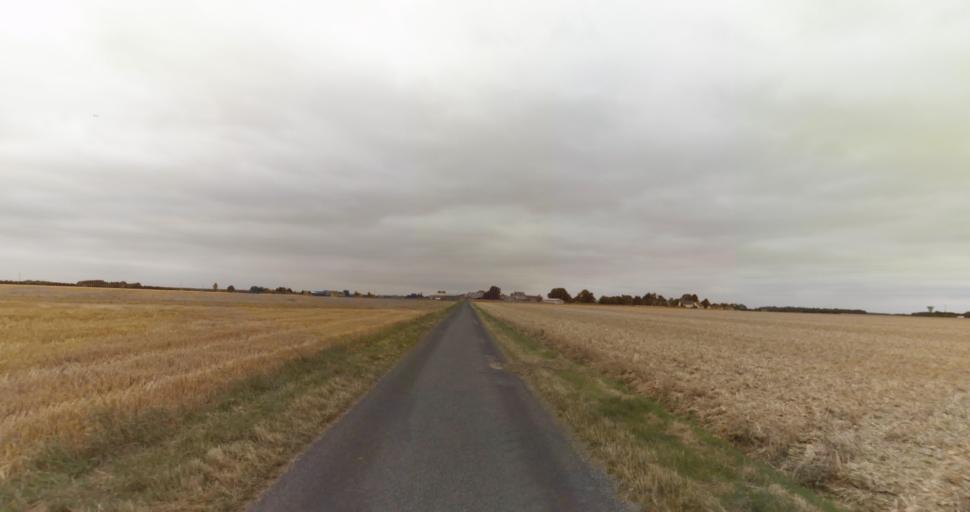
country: FR
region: Haute-Normandie
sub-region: Departement de l'Eure
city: La Couture-Boussey
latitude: 48.9346
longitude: 1.3303
